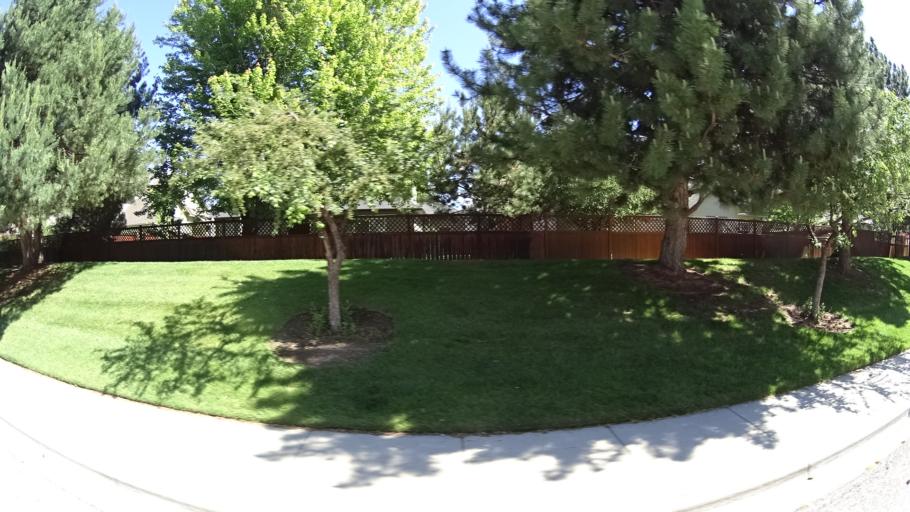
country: US
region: Idaho
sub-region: Ada County
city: Boise
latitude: 43.5512
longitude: -116.1256
